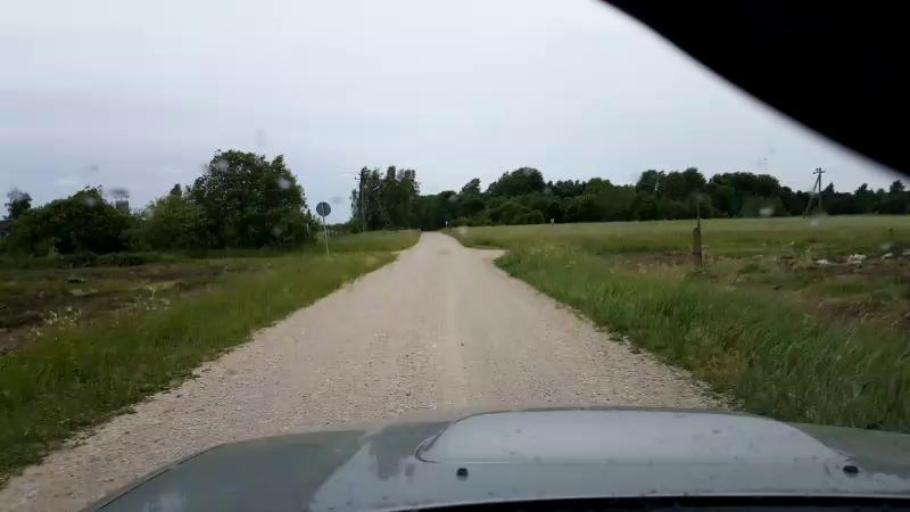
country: EE
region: Paernumaa
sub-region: Halinga vald
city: Parnu-Jaagupi
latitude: 58.5321
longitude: 24.5893
